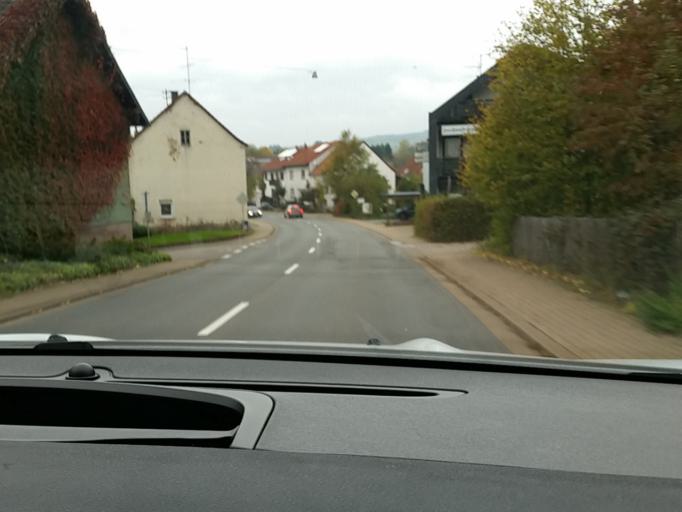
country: DE
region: Saarland
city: Weiskirchen
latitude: 49.5405
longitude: 6.8004
